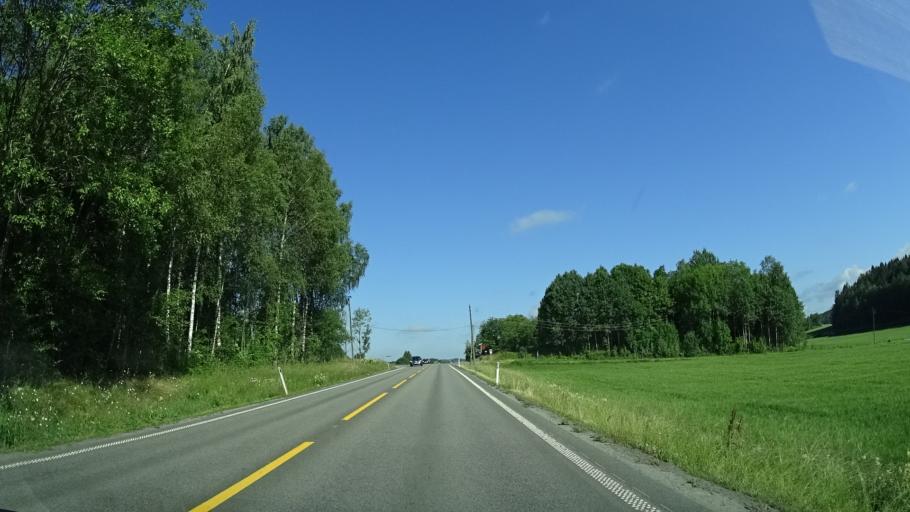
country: NO
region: Ostfold
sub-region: Hobol
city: Elvestad
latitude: 59.6667
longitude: 10.9031
